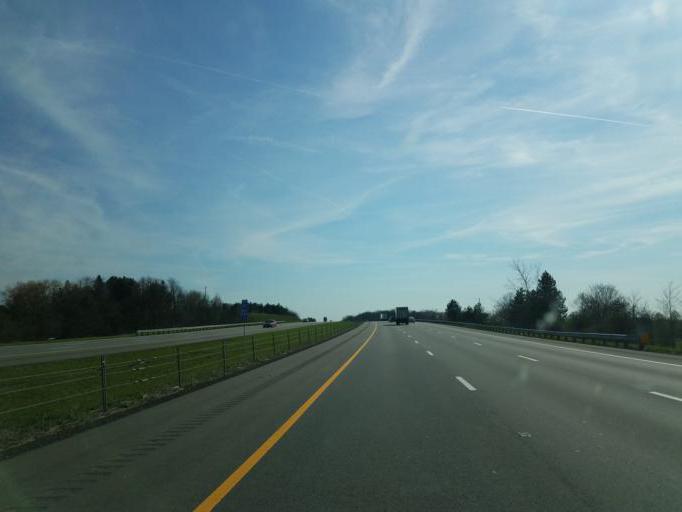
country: US
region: Ohio
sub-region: Morrow County
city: Cardington
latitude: 40.4338
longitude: -82.8130
